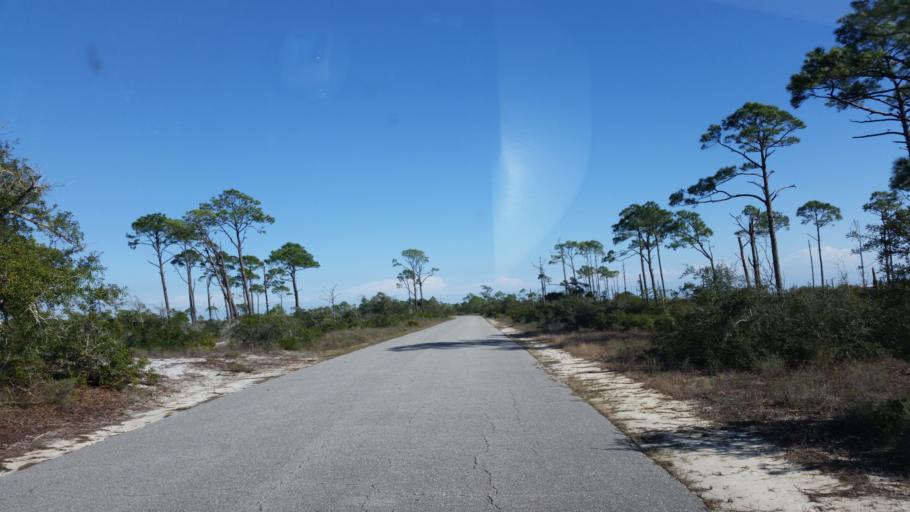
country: US
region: Florida
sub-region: Escambia County
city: Myrtle Grove
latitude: 30.3108
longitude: -87.4121
